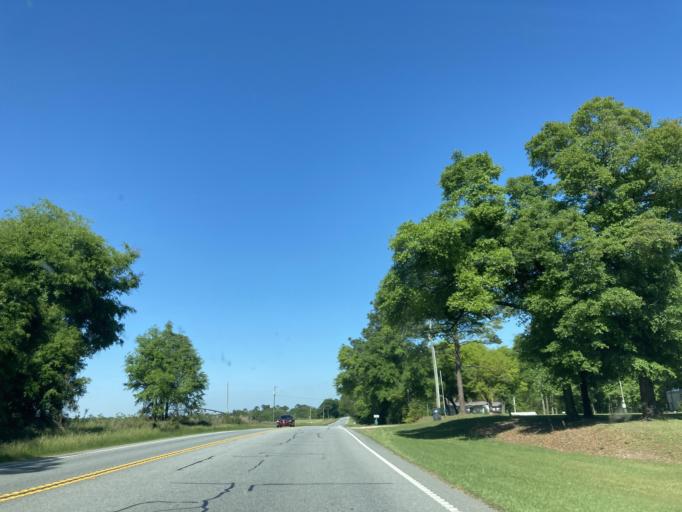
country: US
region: Georgia
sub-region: Baker County
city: Newton
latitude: 31.2507
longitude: -84.4259
